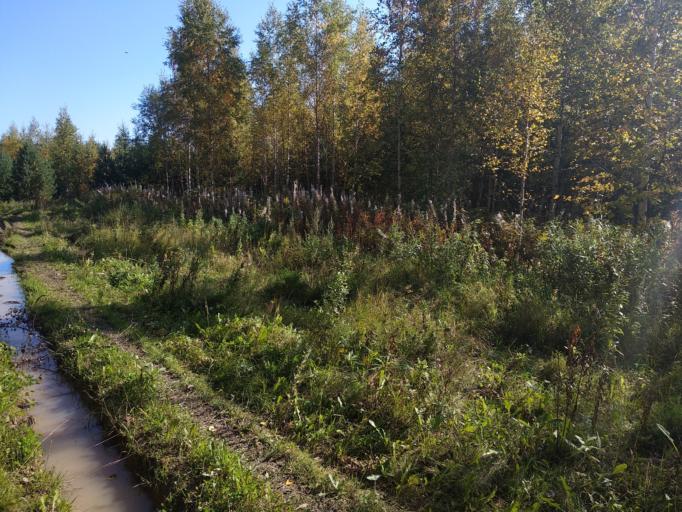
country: RU
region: Sverdlovsk
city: Serov
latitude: 59.7408
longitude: 60.5822
